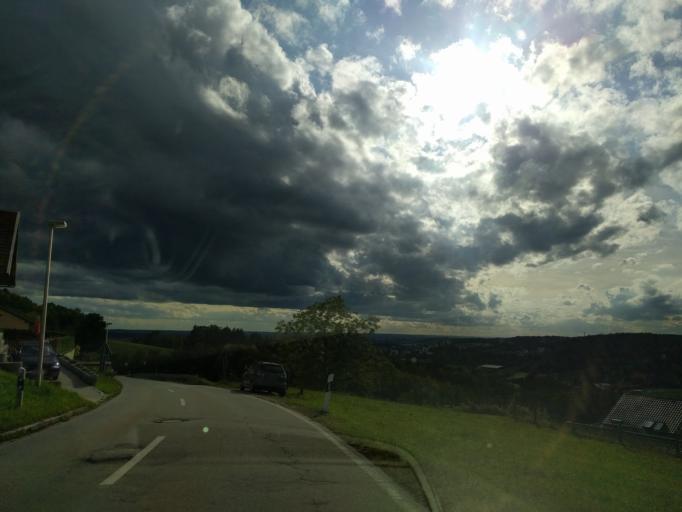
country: DE
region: Bavaria
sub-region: Lower Bavaria
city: Deggendorf
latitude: 48.8598
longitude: 12.9711
